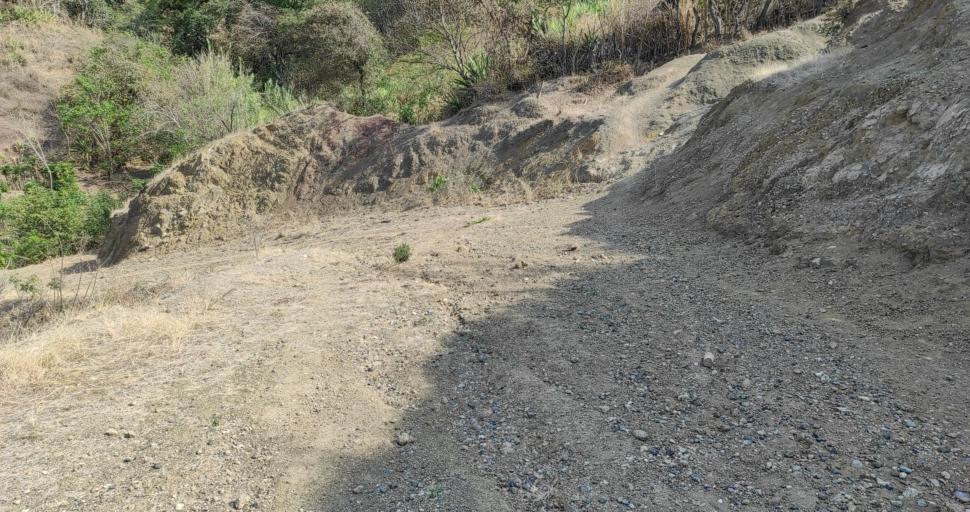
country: EC
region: Loja
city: Catacocha
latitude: -3.9998
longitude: -79.7150
